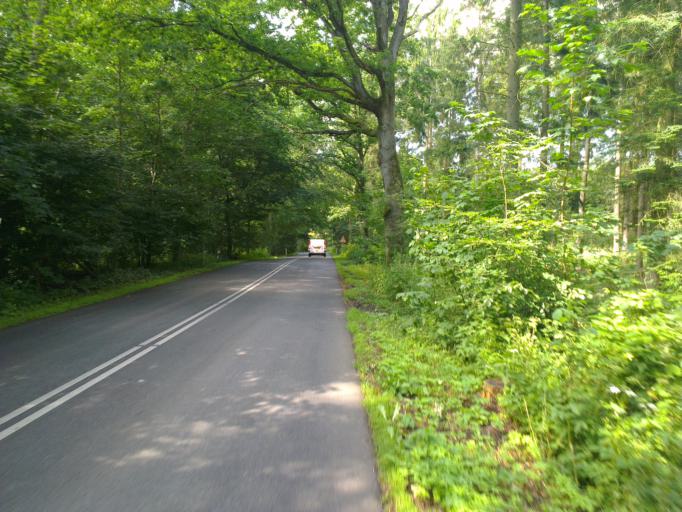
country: DK
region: Zealand
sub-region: Lejre Kommune
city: Ejby
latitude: 55.7344
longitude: 11.8836
